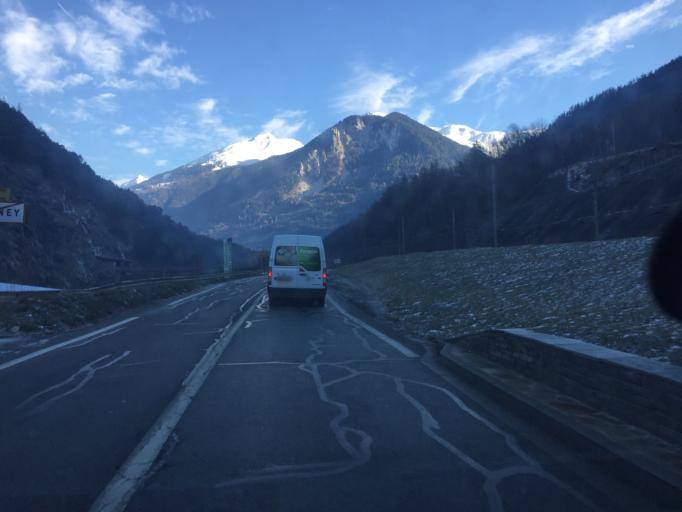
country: FR
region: Rhone-Alpes
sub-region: Departement de la Savoie
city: Modane
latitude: 45.1941
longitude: 6.6304
